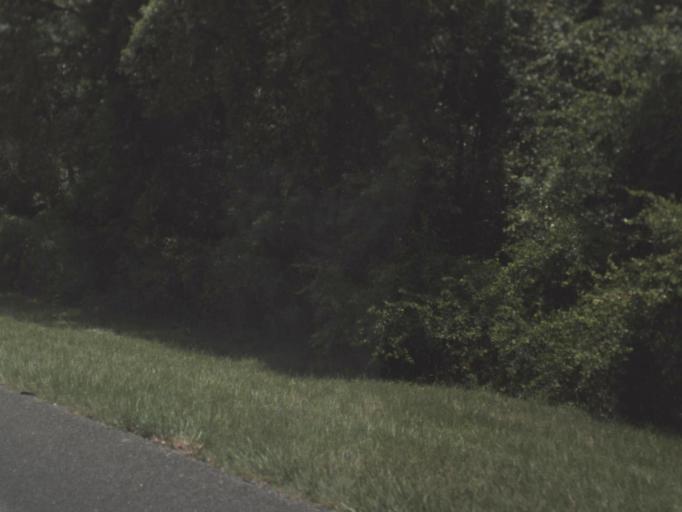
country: US
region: Florida
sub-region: Levy County
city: Manatee Road
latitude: 29.5550
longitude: -82.9030
